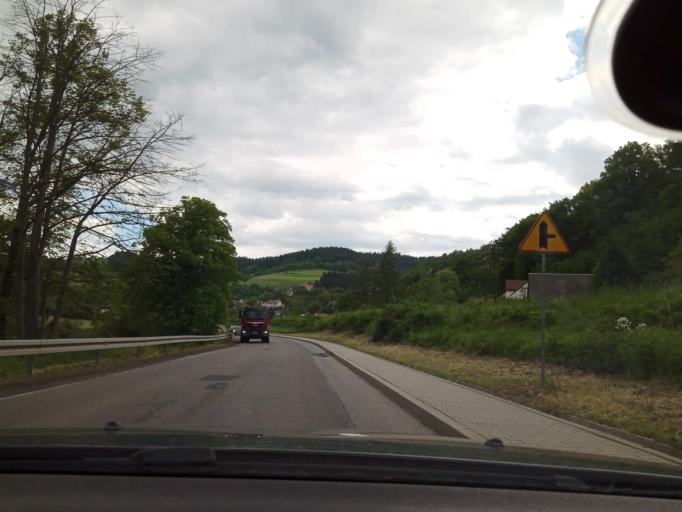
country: PL
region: Lesser Poland Voivodeship
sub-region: Powiat limanowski
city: Tymbark
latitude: 49.7445
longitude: 20.3687
